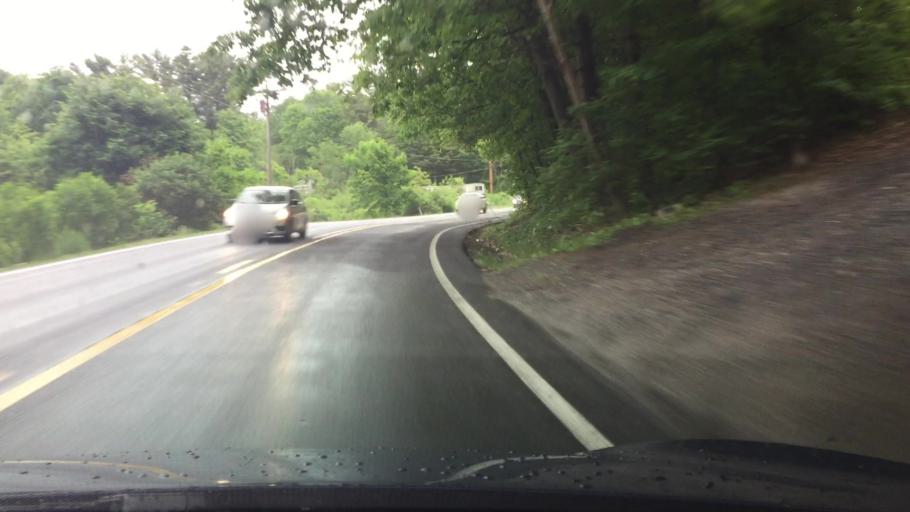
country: US
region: West Virginia
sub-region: Raleigh County
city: Shady Spring
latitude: 37.6931
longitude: -81.0680
